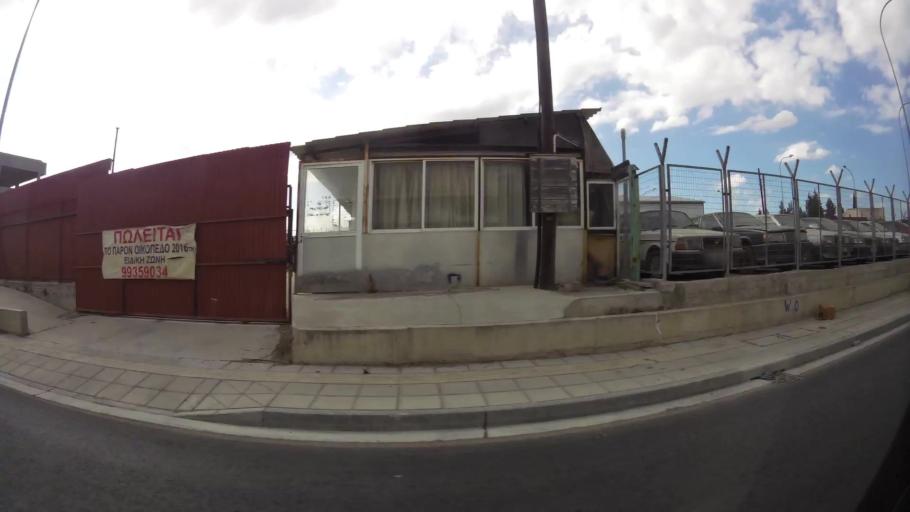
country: CY
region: Lefkosia
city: Nicosia
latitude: 35.1828
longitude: 33.3942
